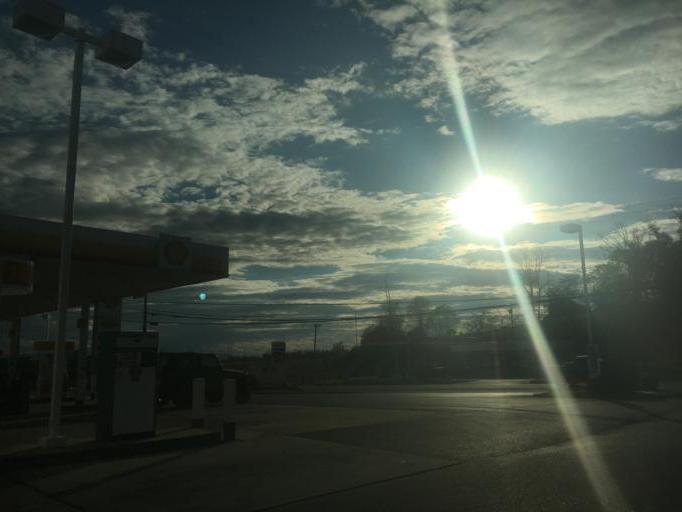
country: US
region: Virginia
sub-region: Washington County
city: Glade Spring
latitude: 36.7737
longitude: -81.7806
